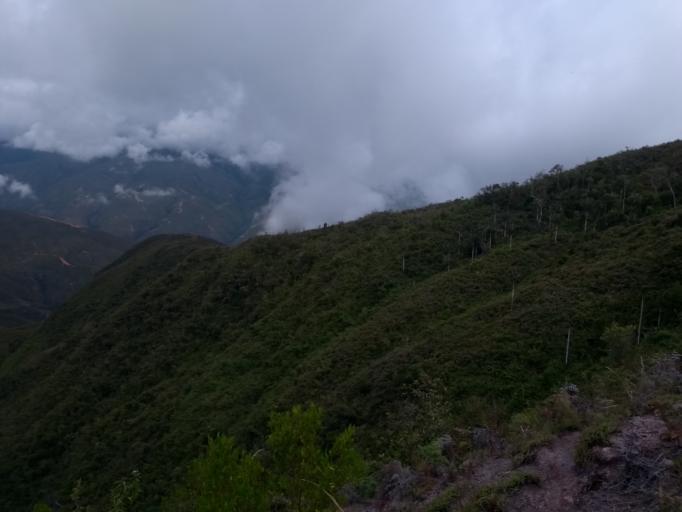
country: CO
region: Cesar
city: Manaure Balcon del Cesar
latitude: 10.1881
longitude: -73.0028
